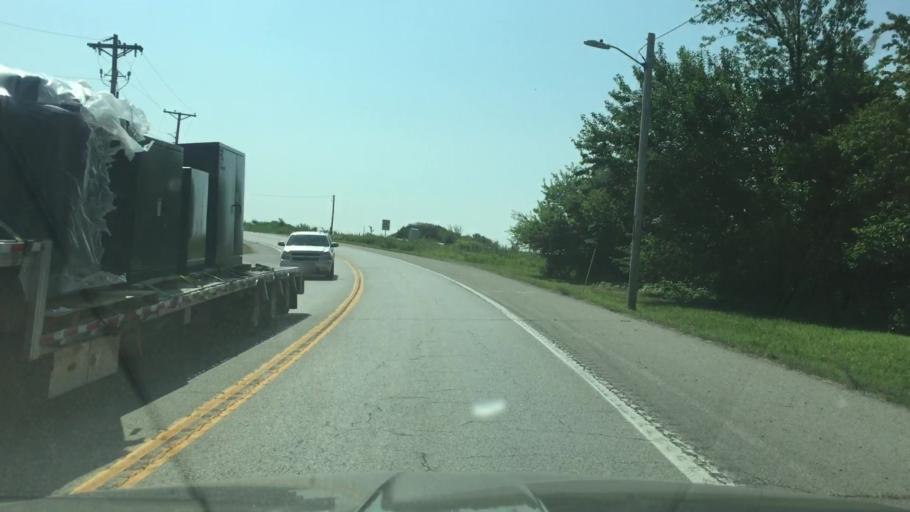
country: US
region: Missouri
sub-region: Pettis County
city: Sedalia
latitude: 38.6973
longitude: -93.1815
